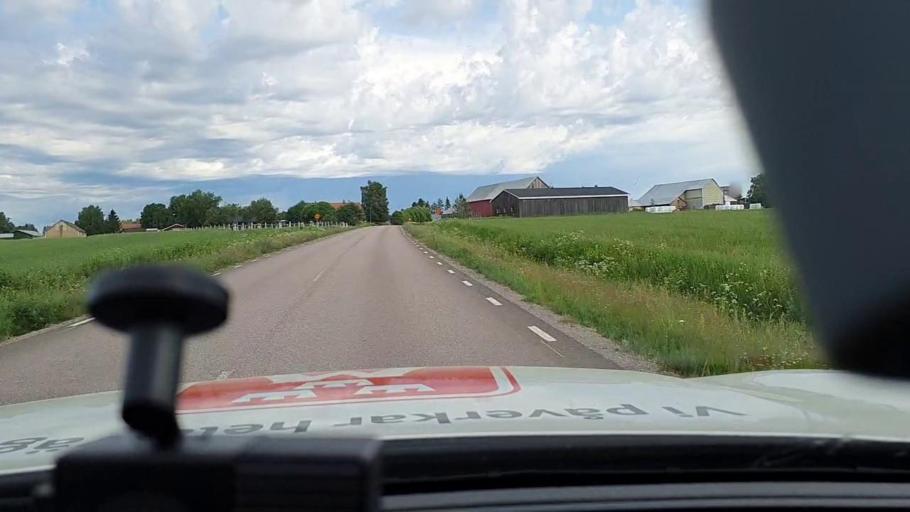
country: SE
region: Norrbotten
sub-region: Bodens Kommun
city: Saevast
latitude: 65.7071
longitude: 21.7619
